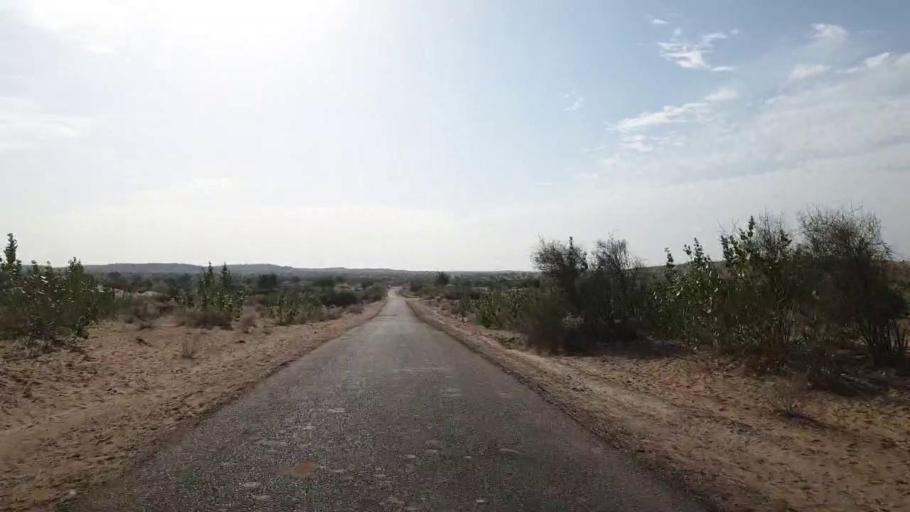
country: PK
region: Sindh
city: Nabisar
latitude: 25.0399
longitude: 70.0004
